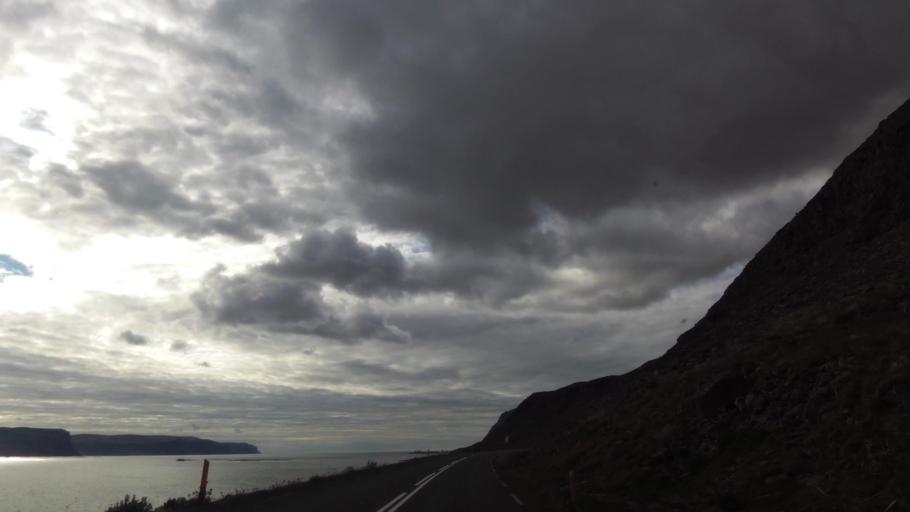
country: IS
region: West
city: Olafsvik
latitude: 65.5719
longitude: -23.9366
